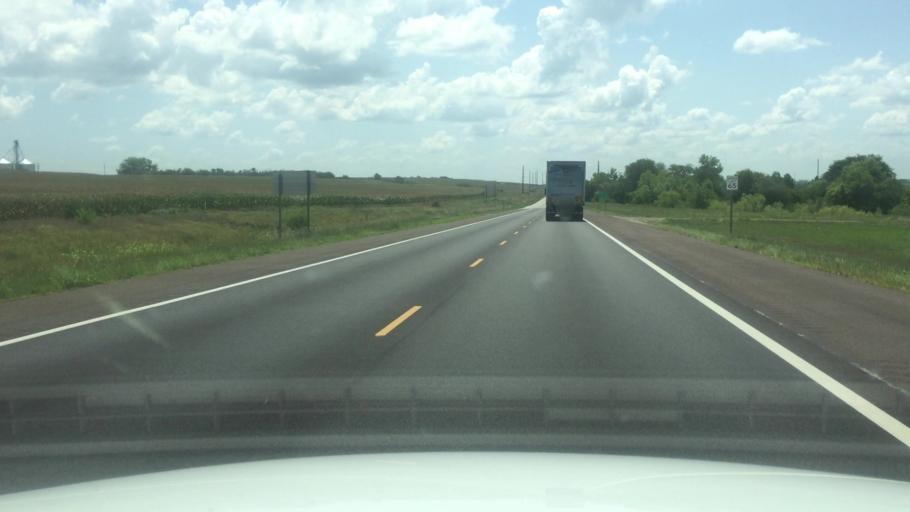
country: US
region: Kansas
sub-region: Nemaha County
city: Sabetha
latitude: 39.8330
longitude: -95.7333
